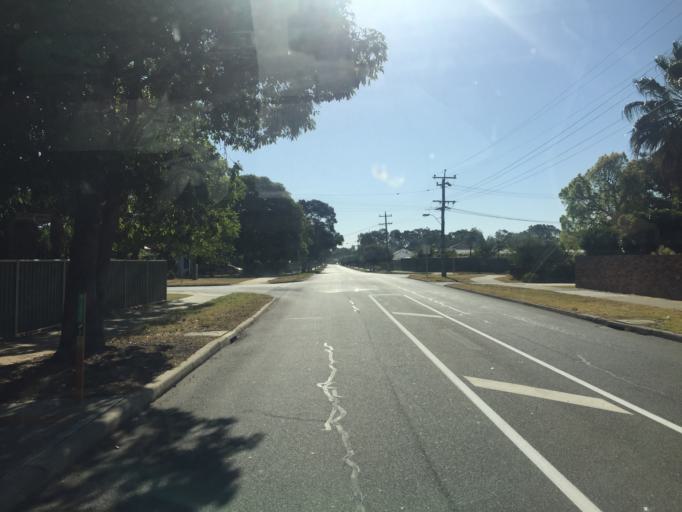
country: AU
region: Western Australia
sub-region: Gosnells
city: Kenwick
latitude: -32.0348
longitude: 115.9760
